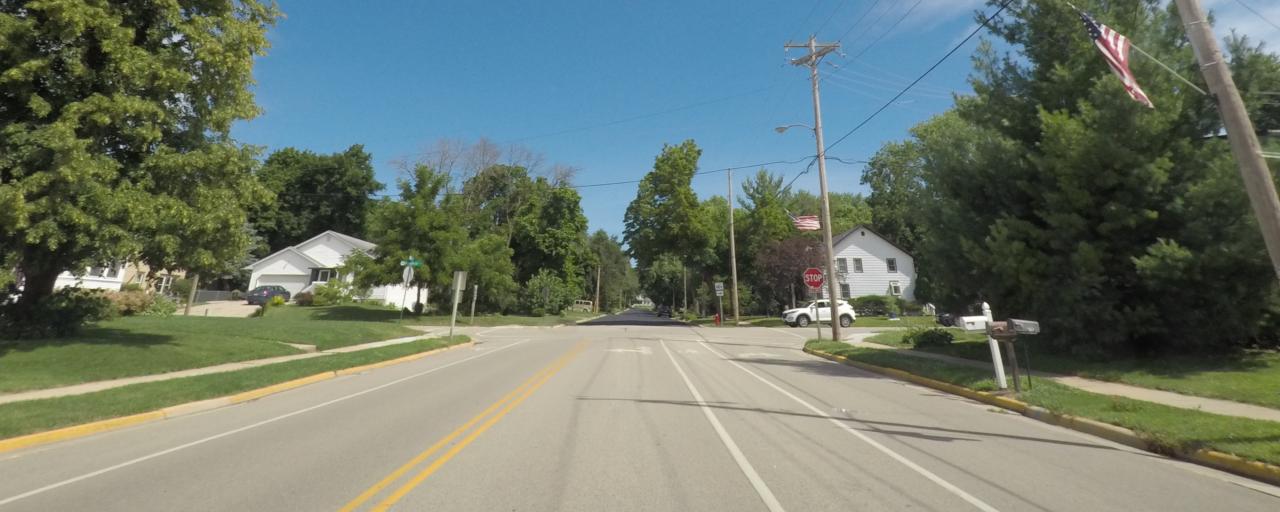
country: US
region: Wisconsin
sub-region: Dane County
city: McFarland
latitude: 43.0151
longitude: -89.2887
